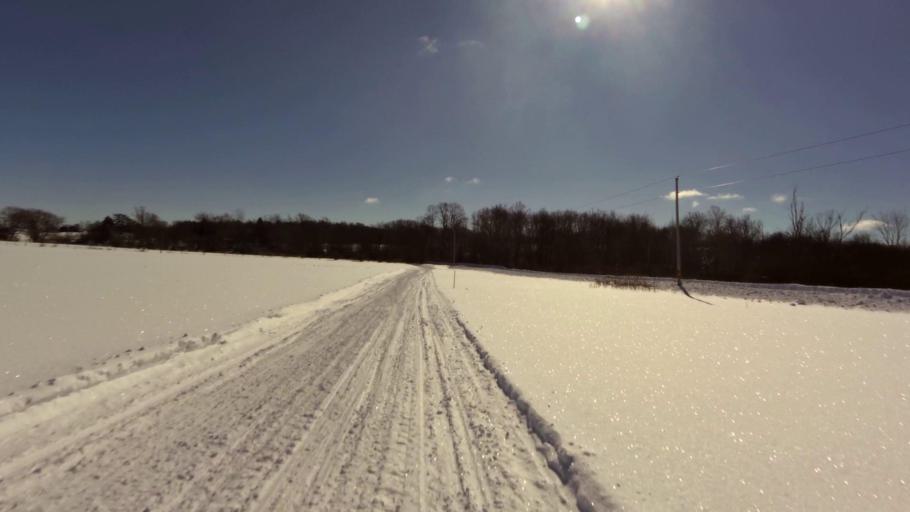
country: US
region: New York
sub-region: Chautauqua County
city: Fredonia
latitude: 42.3663
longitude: -79.1734
